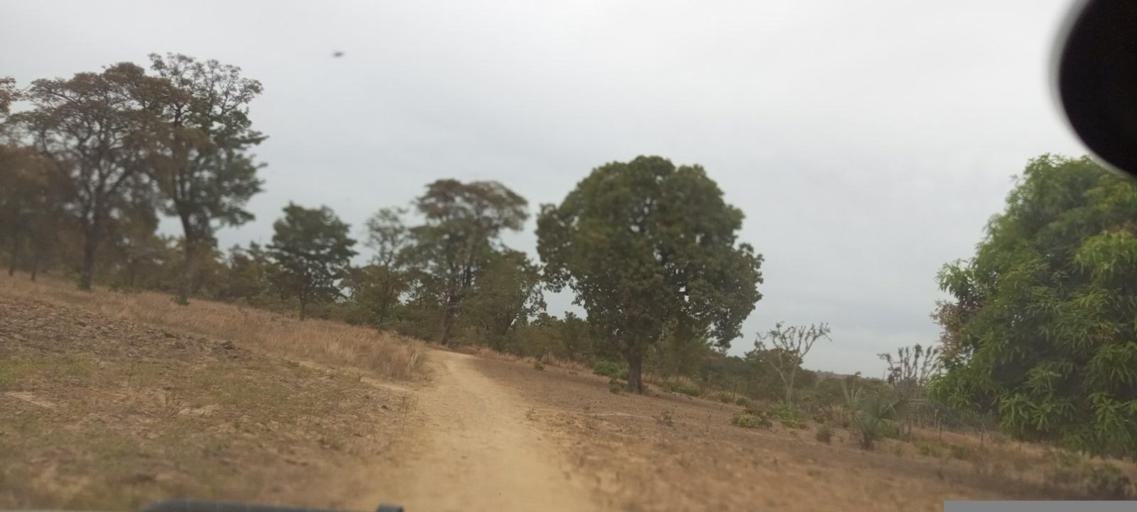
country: ML
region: Koulikoro
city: Kati
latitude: 12.7702
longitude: -8.3723
